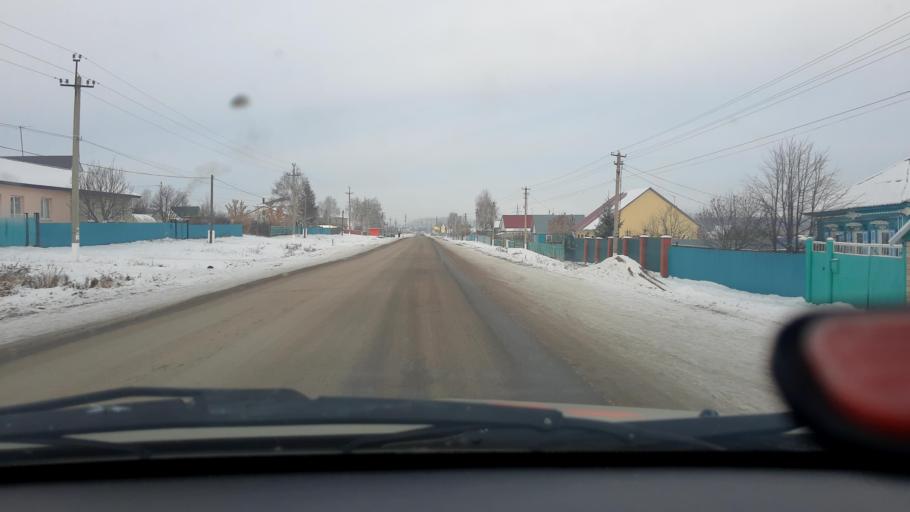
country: RU
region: Bashkortostan
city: Avdon
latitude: 54.4144
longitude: 55.8078
